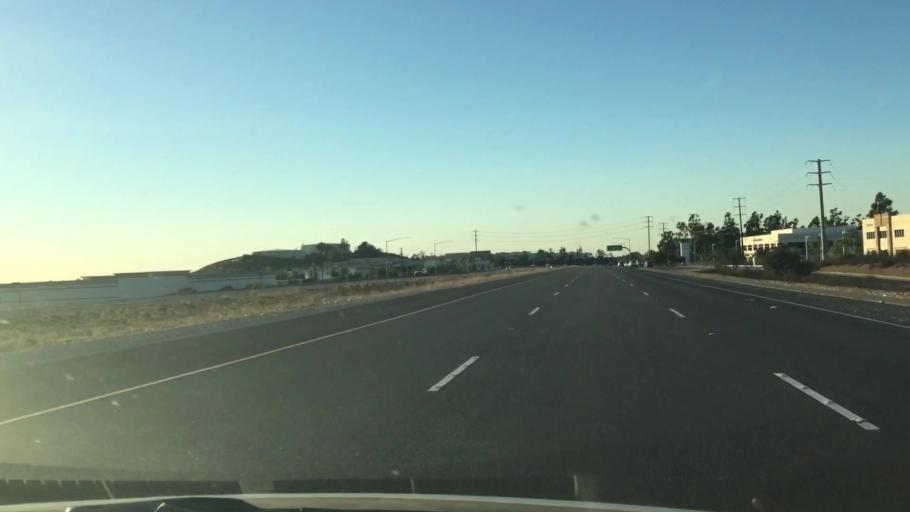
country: US
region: California
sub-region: Orange County
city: Foothill Ranch
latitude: 33.6723
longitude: -117.6615
